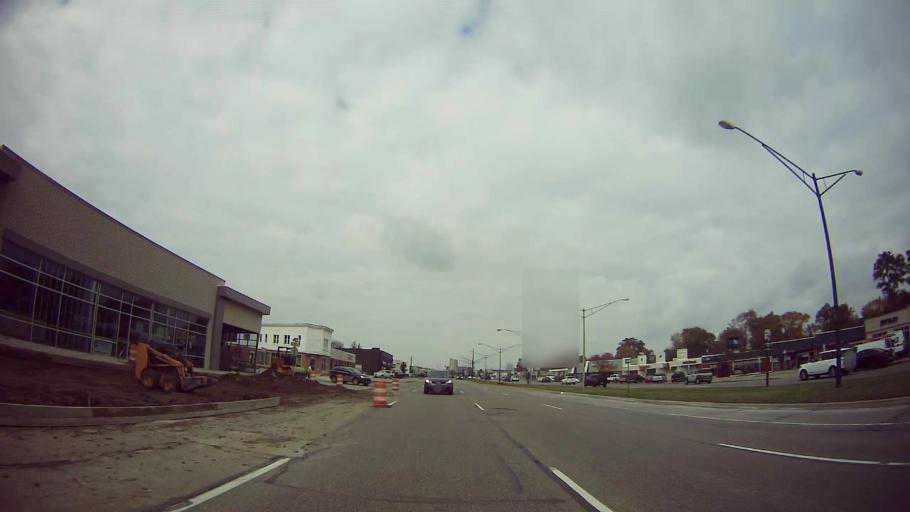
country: US
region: Michigan
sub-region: Oakland County
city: Birmingham
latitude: 42.5341
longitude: -83.2021
